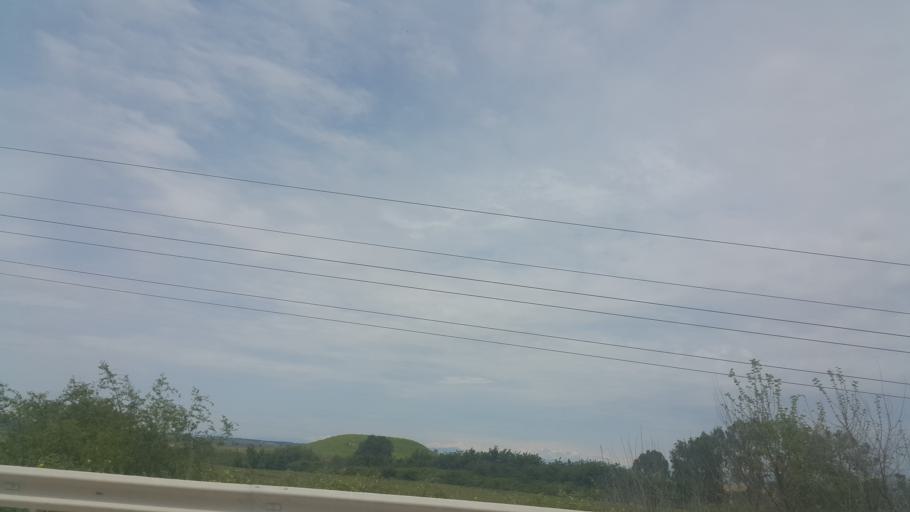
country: TR
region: Adana
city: Ceyhan
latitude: 37.0167
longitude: 35.7151
